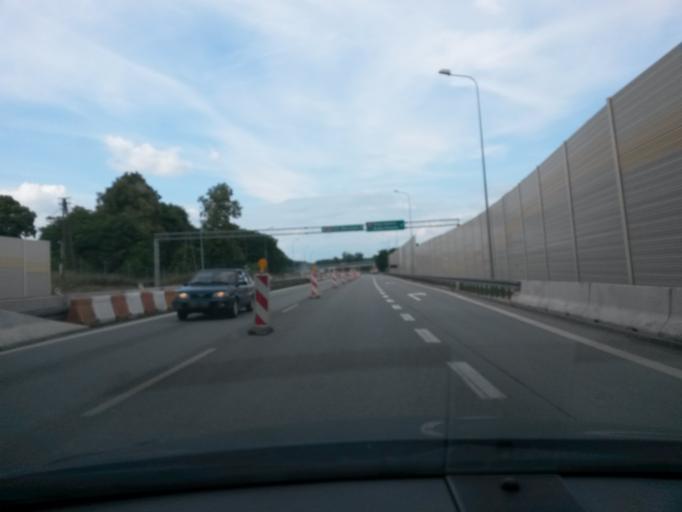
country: PL
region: Lodz Voivodeship
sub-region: Powiat skierniewicki
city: Kowiesy
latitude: 51.9162
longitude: 20.4519
